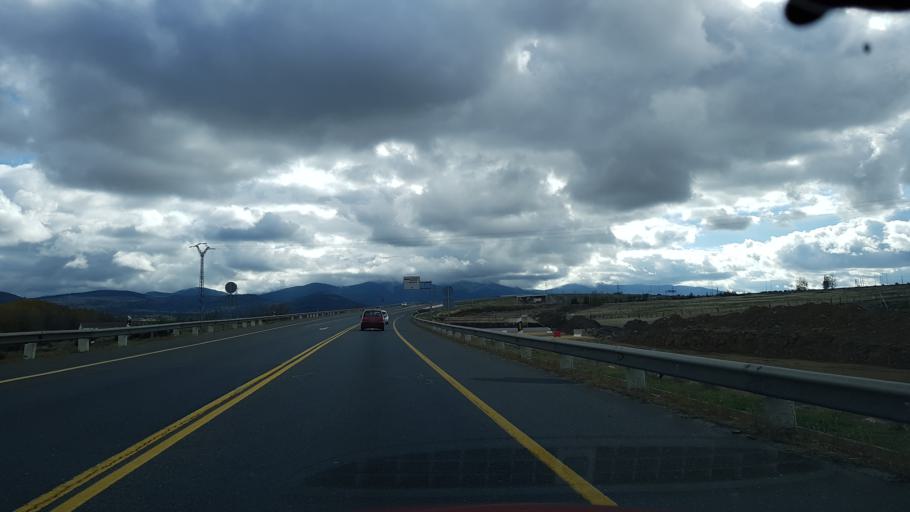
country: ES
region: Castille and Leon
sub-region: Provincia de Segovia
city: San Cristobal de Segovia
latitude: 40.9330
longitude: -4.0853
